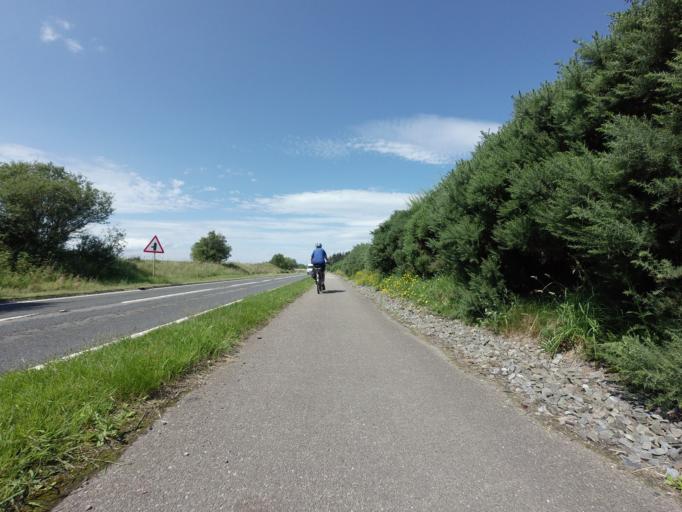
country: GB
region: Scotland
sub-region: Highland
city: Conon Bridge
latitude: 57.5445
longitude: -4.3822
